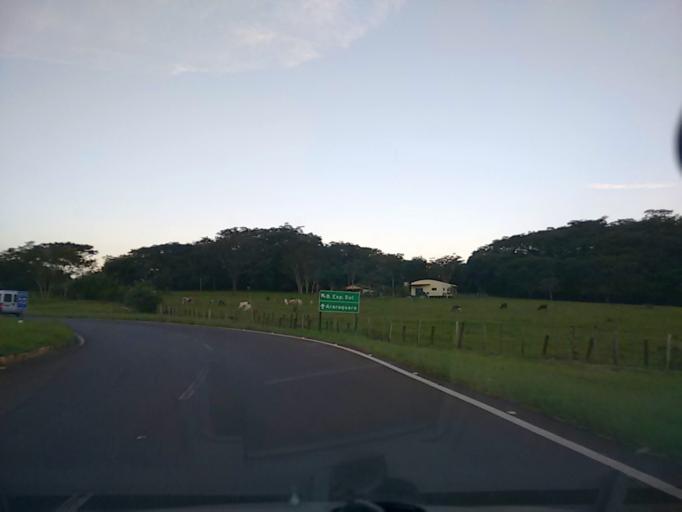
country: BR
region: Sao Paulo
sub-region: Boa Esperanca Do Sul
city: Boa Esperanca do Sul
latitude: -21.9893
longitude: -48.3754
